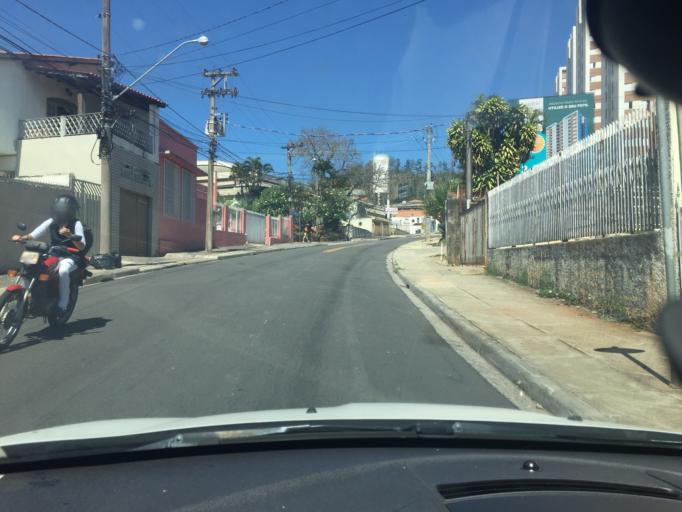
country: BR
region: Sao Paulo
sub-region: Jundiai
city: Jundiai
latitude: -23.2109
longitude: -46.8861
